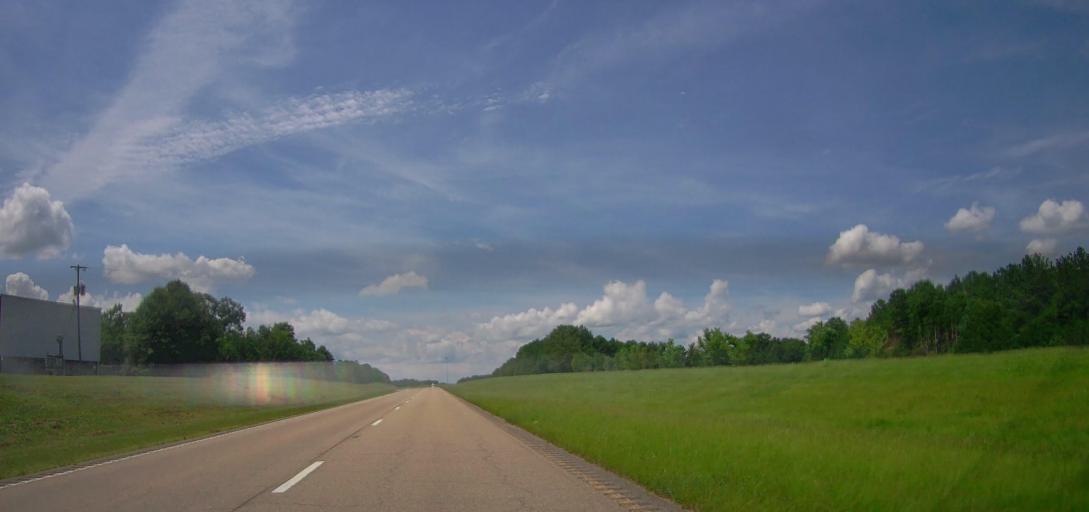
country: US
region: Mississippi
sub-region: Lee County
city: Nettleton
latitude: 33.9899
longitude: -88.6228
